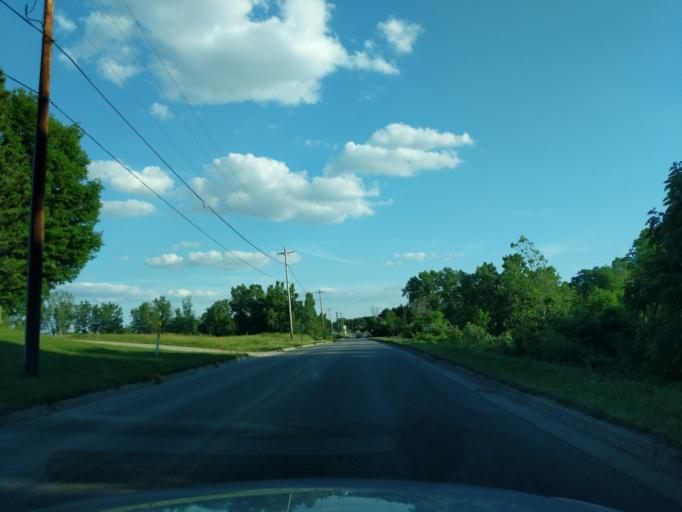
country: US
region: Indiana
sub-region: Huntington County
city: Huntington
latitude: 40.8679
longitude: -85.4709
